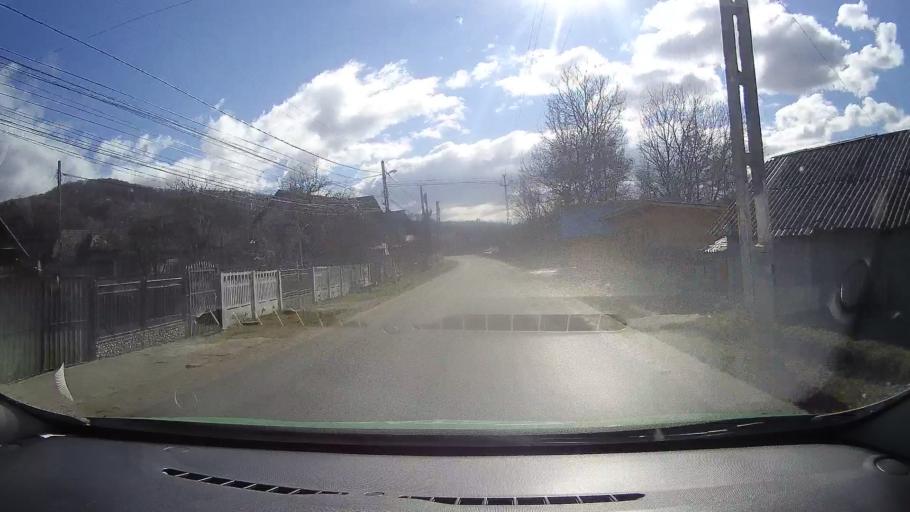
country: RO
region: Dambovita
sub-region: Comuna Runcu
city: Badeni
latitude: 45.1566
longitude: 25.3987
